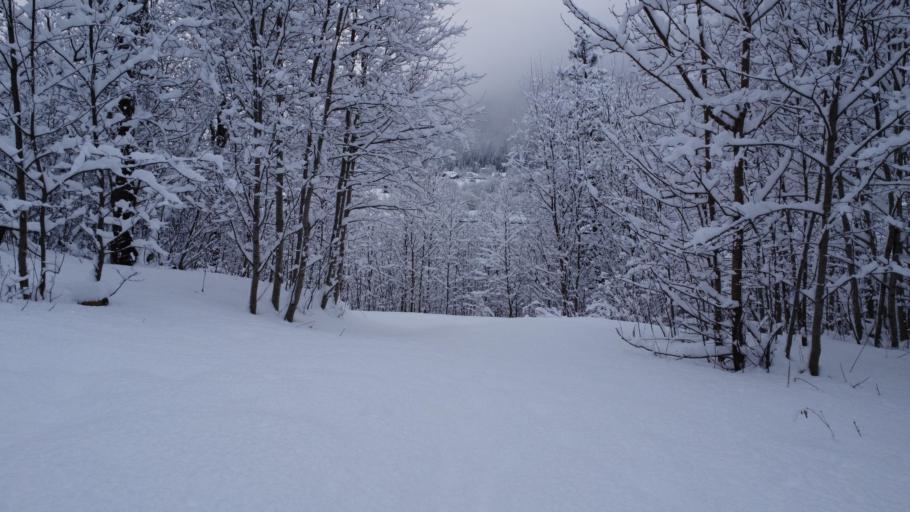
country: NO
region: Nordland
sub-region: Rana
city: Mo i Rana
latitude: 66.3332
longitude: 14.1642
